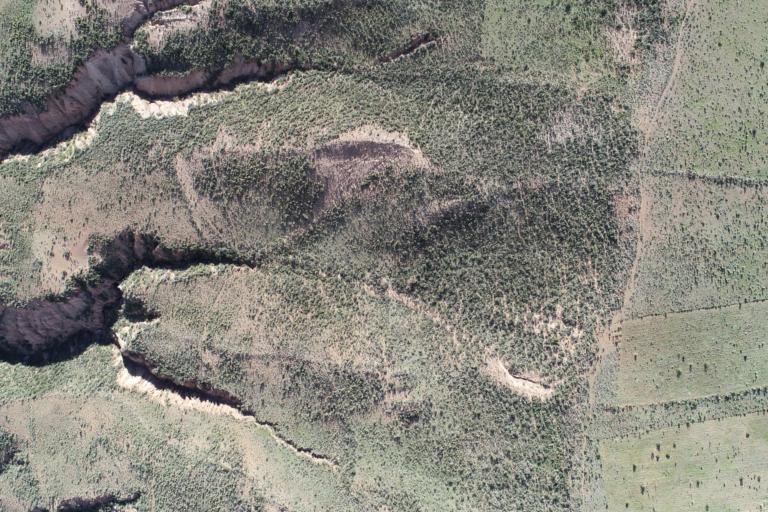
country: BO
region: La Paz
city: Curahuara de Carangas
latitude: -17.3006
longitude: -68.4937
